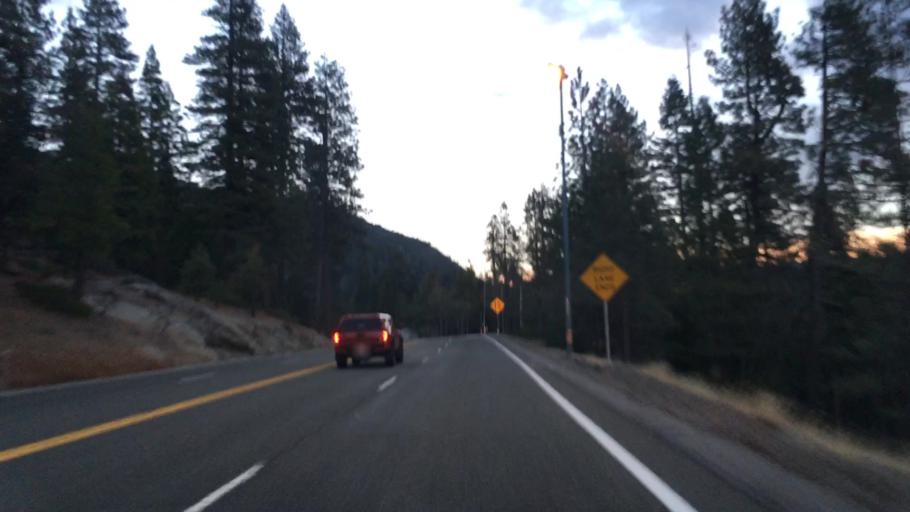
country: US
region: California
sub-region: El Dorado County
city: South Lake Tahoe
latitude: 38.7885
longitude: -120.2008
